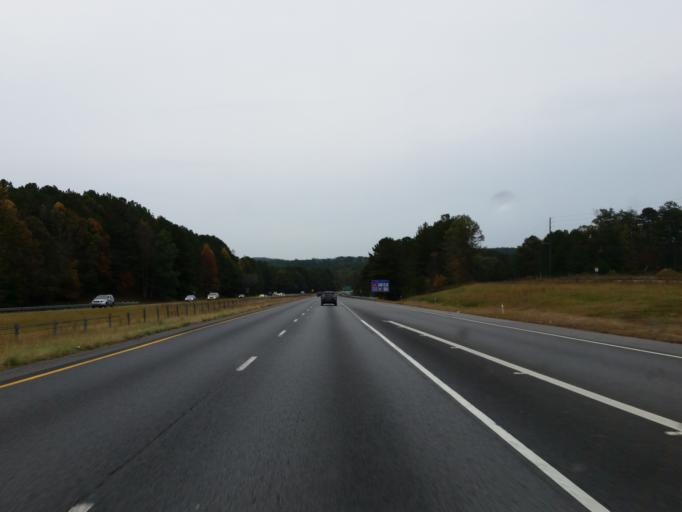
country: US
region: Georgia
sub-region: Cherokee County
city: Woodstock
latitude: 34.1279
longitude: -84.5257
